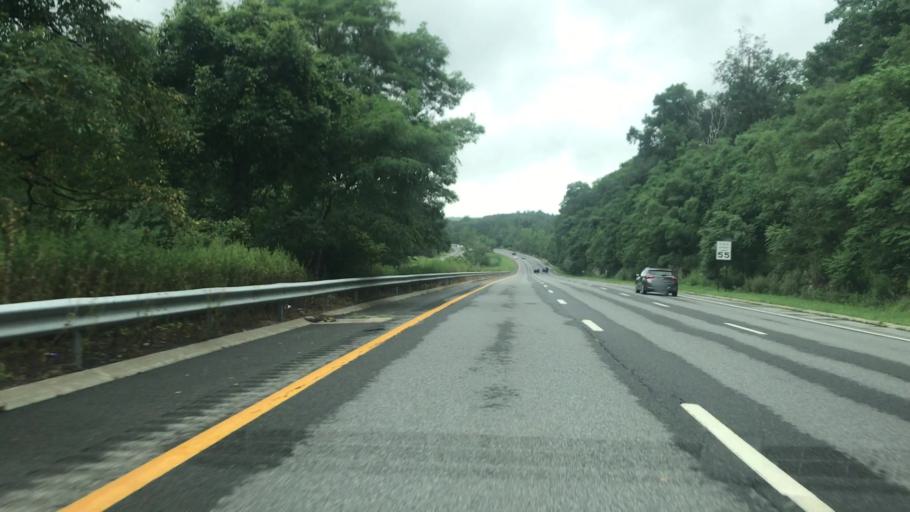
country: US
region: New York
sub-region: Westchester County
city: Briarcliff Manor
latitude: 41.1785
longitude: -73.8086
